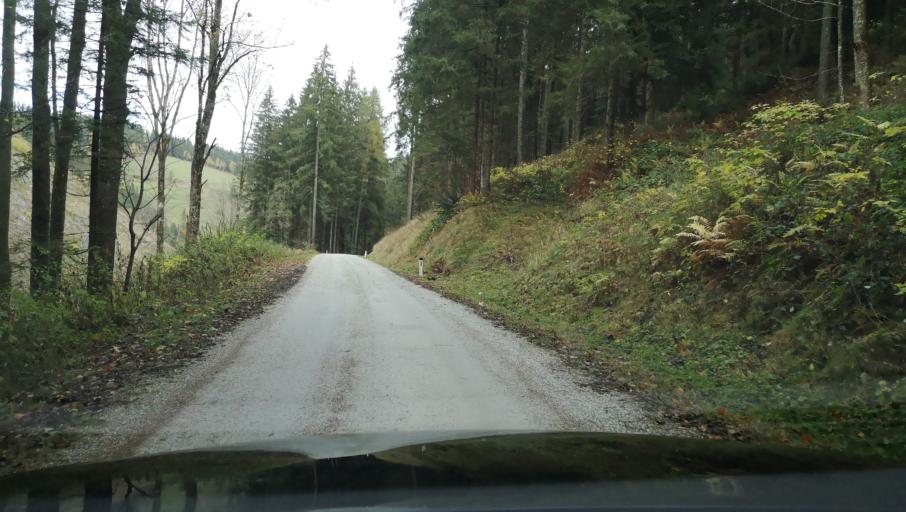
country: AT
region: Styria
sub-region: Politischer Bezirk Weiz
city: Gasen
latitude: 47.3760
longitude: 15.6152
